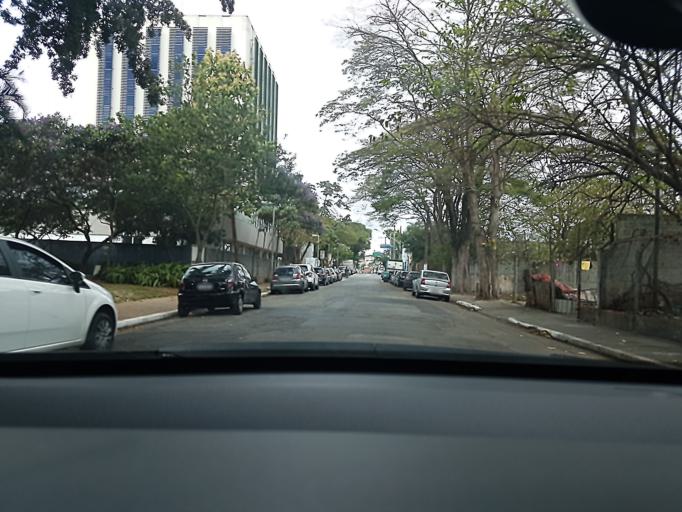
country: BR
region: Sao Paulo
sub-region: Taboao Da Serra
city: Taboao da Serra
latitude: -23.6446
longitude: -46.7091
